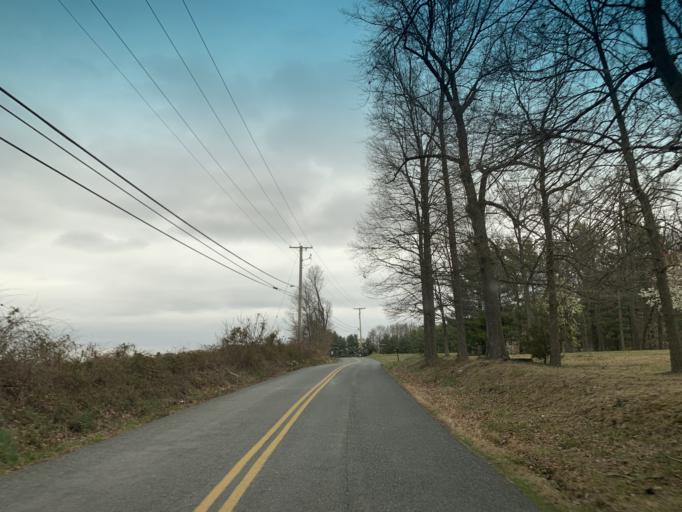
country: US
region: Maryland
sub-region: Harford County
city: Aberdeen
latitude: 39.5579
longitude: -76.1961
